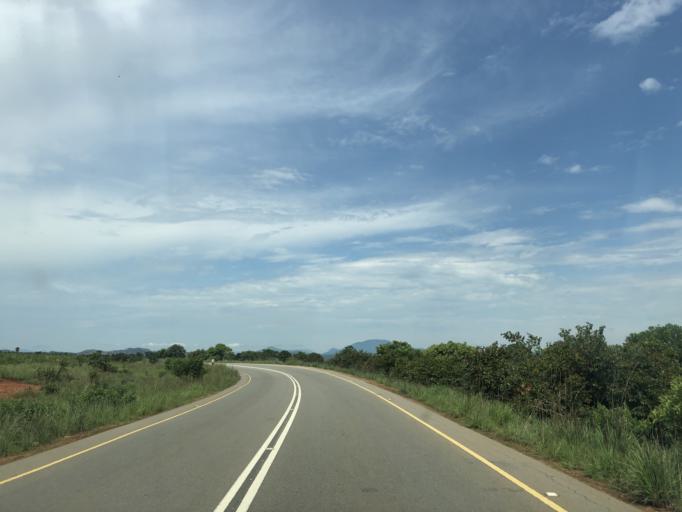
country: AO
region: Cuanza Sul
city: Quibala
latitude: -10.7334
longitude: 15.0206
